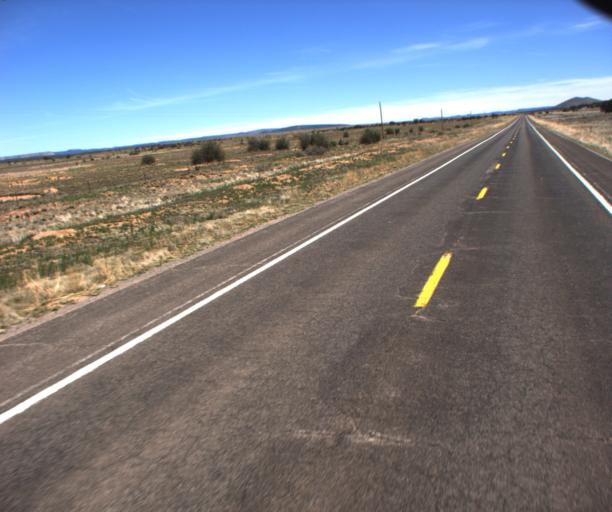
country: US
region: Arizona
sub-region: Mohave County
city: Peach Springs
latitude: 35.5533
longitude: -113.3358
